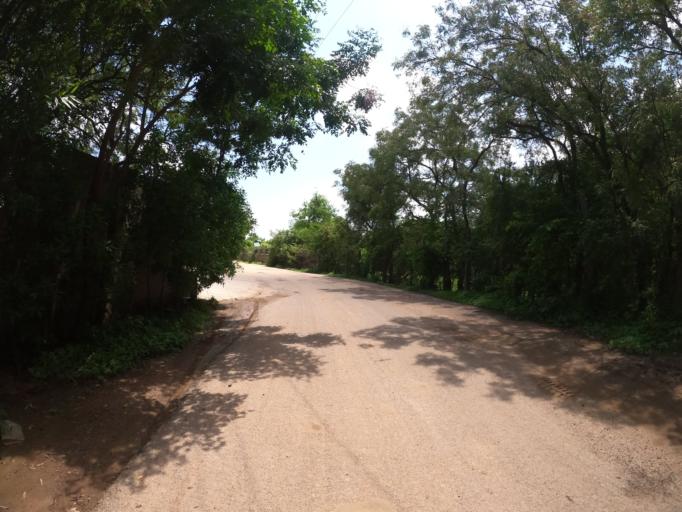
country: IN
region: Telangana
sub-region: Medak
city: Serilingampalle
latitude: 17.3724
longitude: 78.3247
